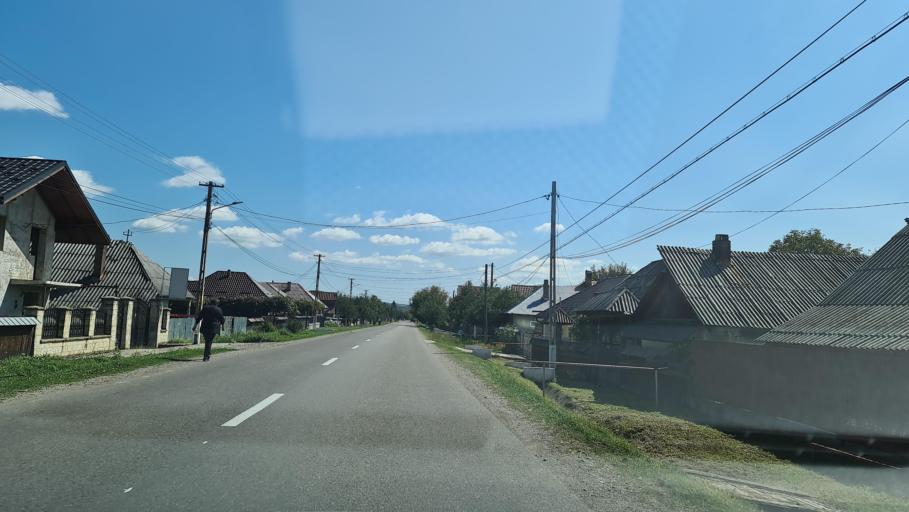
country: RO
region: Bacau
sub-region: Comuna Balcani
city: Frumoasa
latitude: 46.6616
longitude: 26.5421
